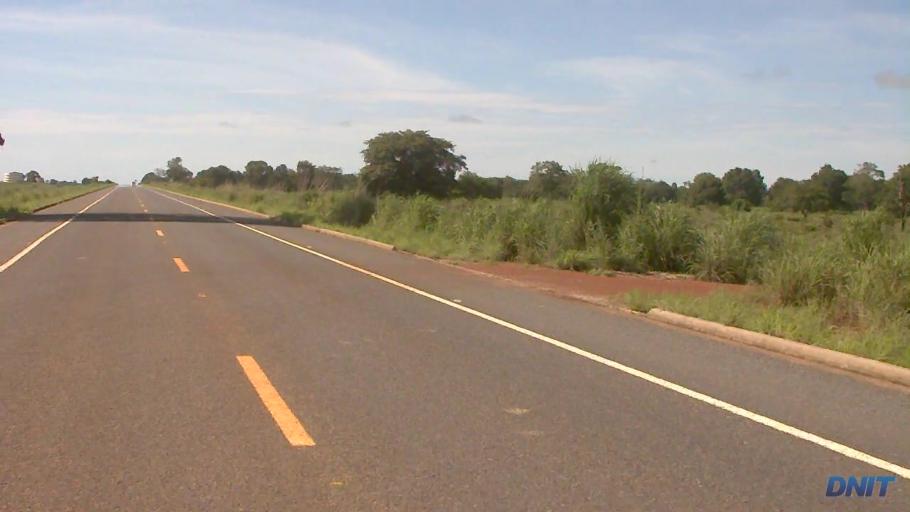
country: BR
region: Goias
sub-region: Sao Miguel Do Araguaia
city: Sao Miguel do Araguaia
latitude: -13.4278
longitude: -50.1272
